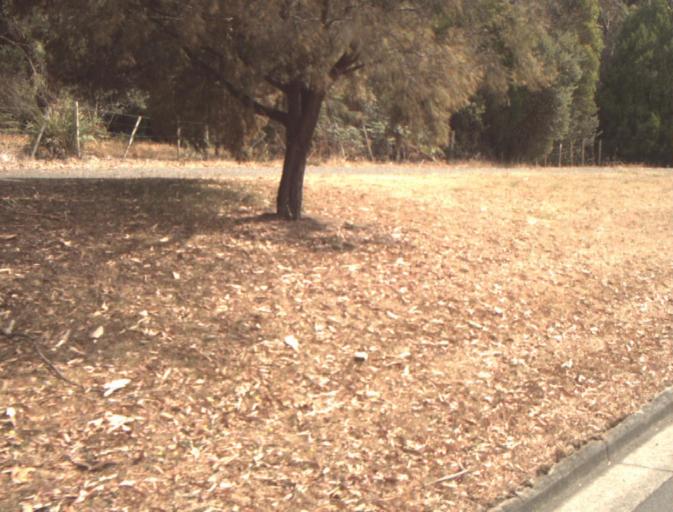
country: AU
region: Tasmania
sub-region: Launceston
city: Newstead
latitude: -41.4702
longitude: 147.1755
